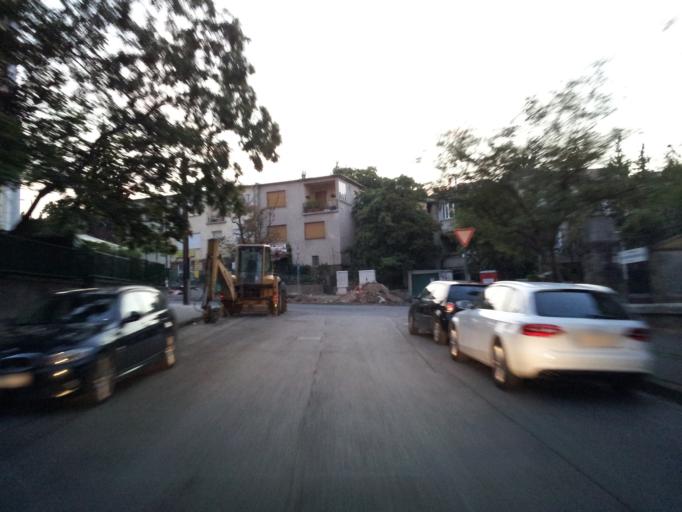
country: HU
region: Budapest
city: Budapest XII. keruelet
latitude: 47.4931
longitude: 19.0133
